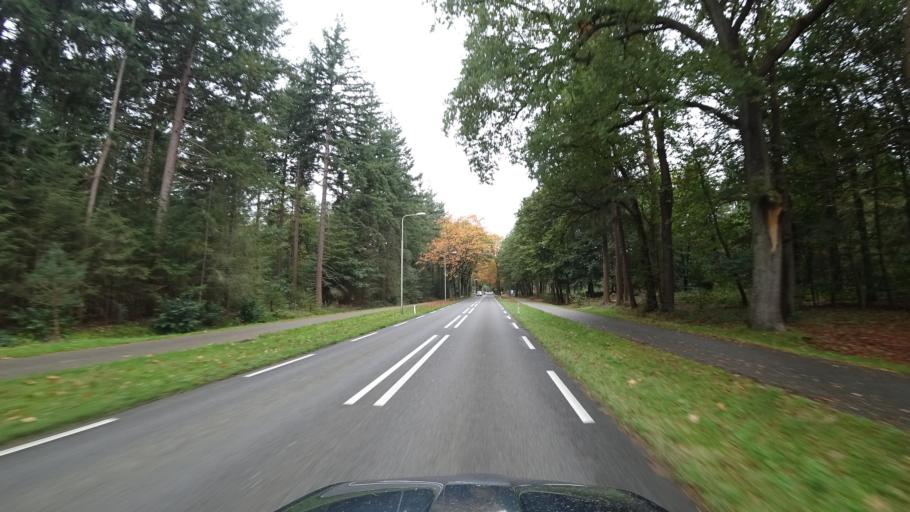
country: NL
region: North Holland
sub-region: Gemeente Hilversum
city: Hilversum
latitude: 52.2053
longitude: 5.2229
